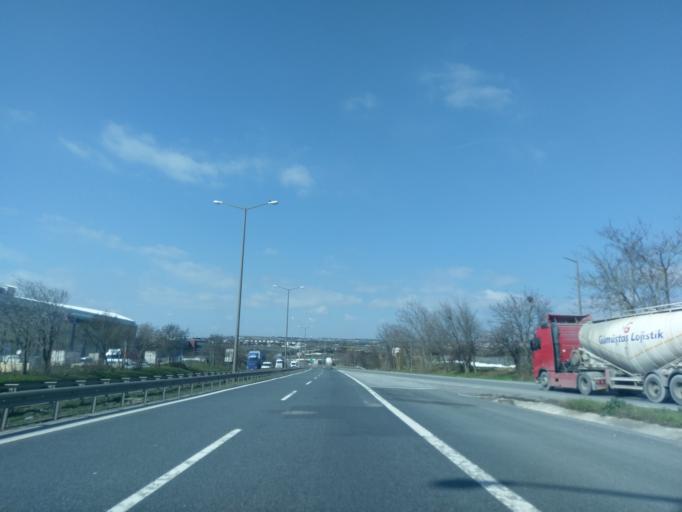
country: TR
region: Istanbul
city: Ortakoy
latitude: 41.0869
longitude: 28.3671
